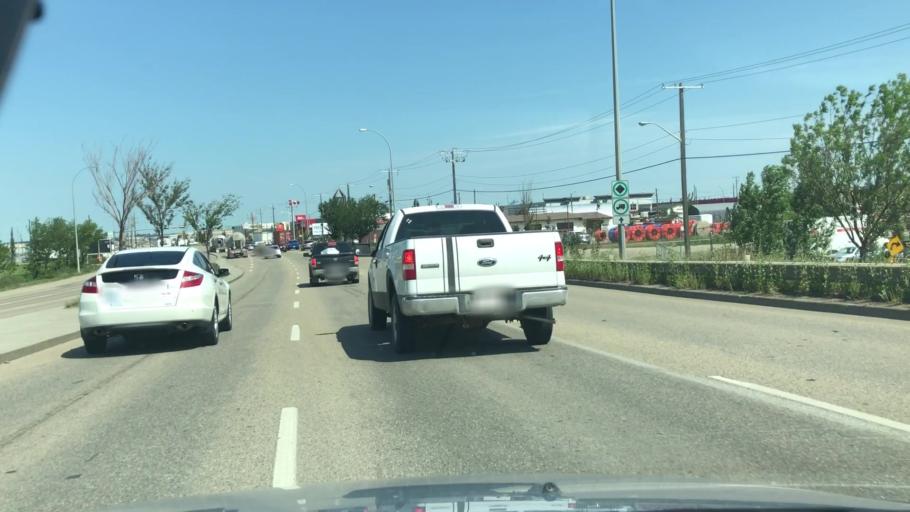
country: CA
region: Alberta
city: St. Albert
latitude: 53.5826
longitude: -113.5906
